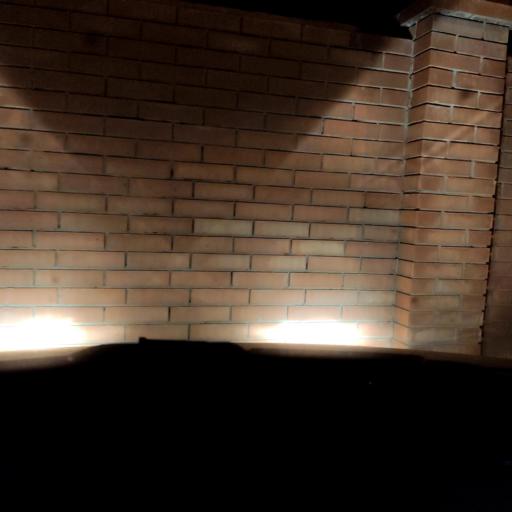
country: RU
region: Samara
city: Tol'yatti
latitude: 53.5402
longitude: 49.4236
